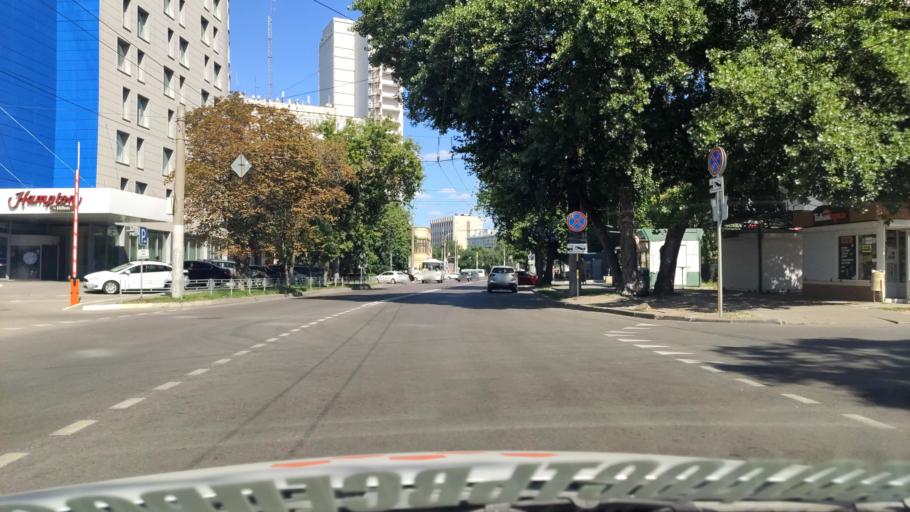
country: RU
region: Voronezj
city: Voronezh
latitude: 51.6743
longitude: 39.1822
